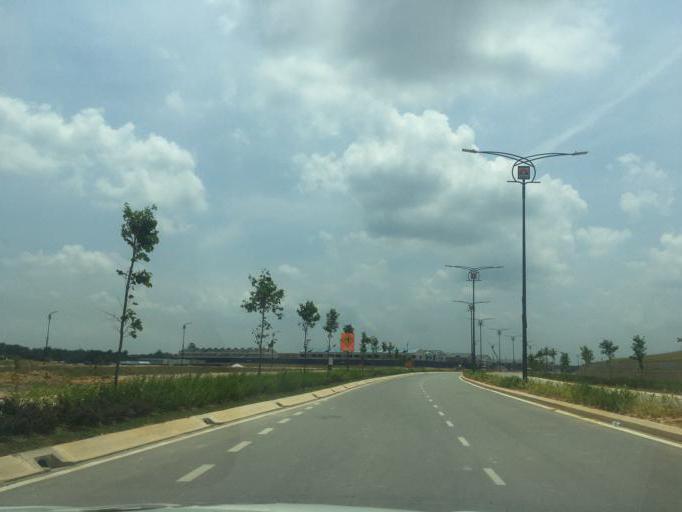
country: MY
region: Putrajaya
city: Putrajaya
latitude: 2.8470
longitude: 101.7061
